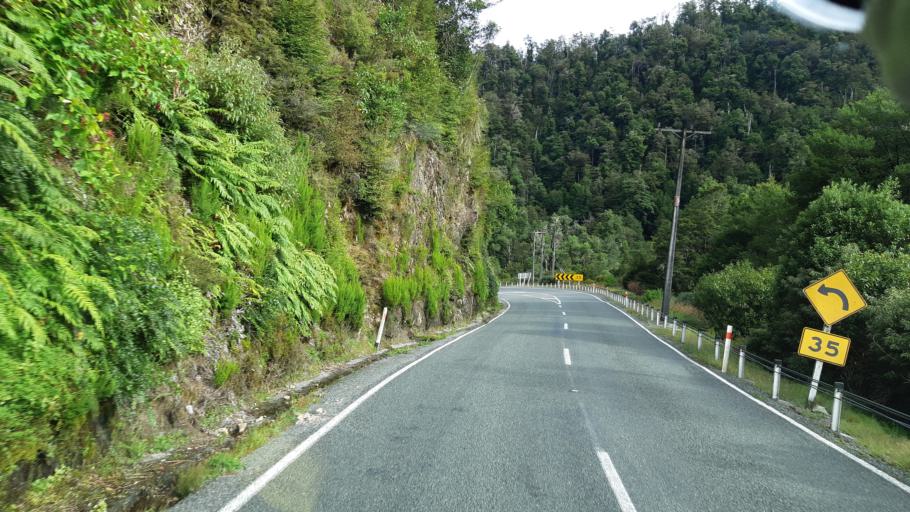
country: NZ
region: West Coast
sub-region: Buller District
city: Westport
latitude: -41.9891
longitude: 172.2182
